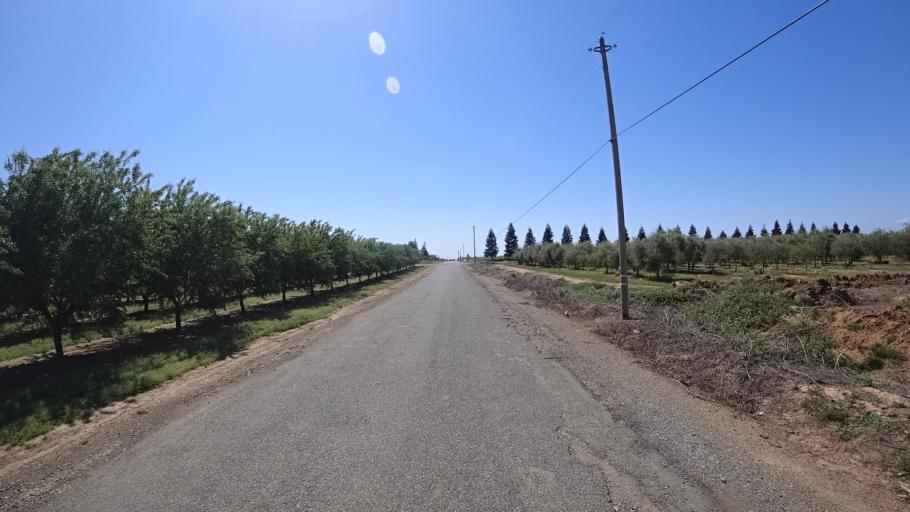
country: US
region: California
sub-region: Glenn County
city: Orland
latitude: 39.7881
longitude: -122.1690
